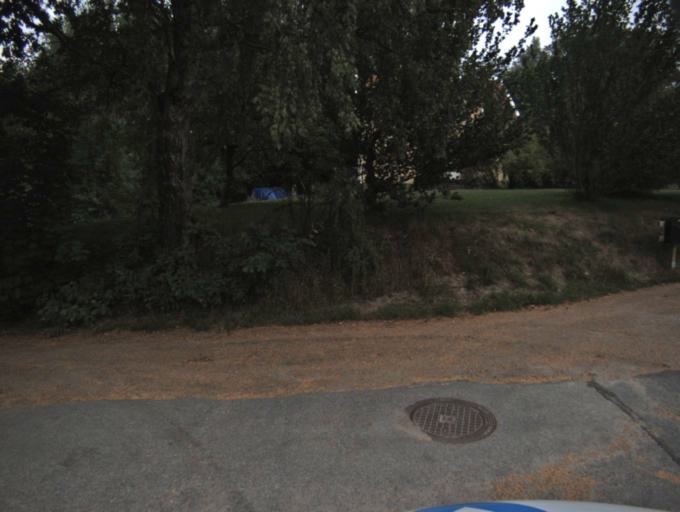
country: SE
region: Vaestra Goetaland
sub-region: Ulricehamns Kommun
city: Ulricehamn
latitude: 57.7439
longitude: 13.4196
